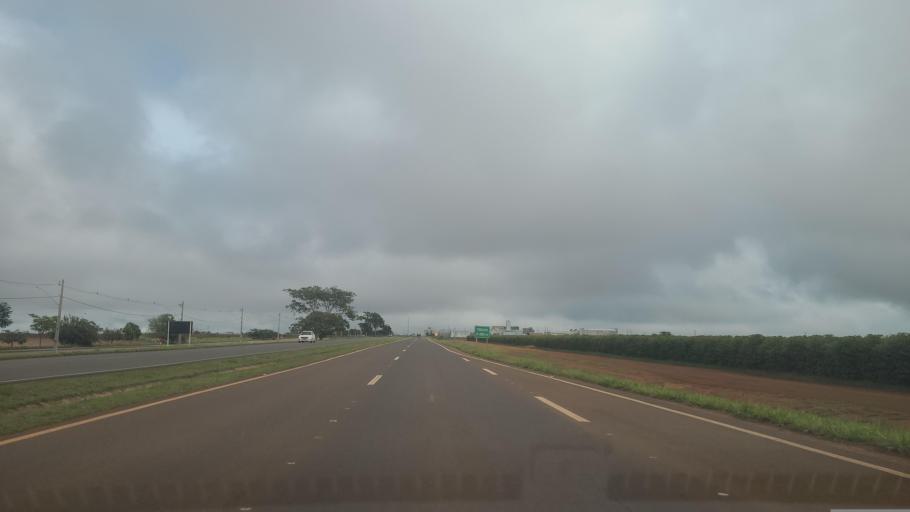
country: BR
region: Minas Gerais
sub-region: Sao Gotardo
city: Sao Gotardo
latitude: -19.2136
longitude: -46.2241
